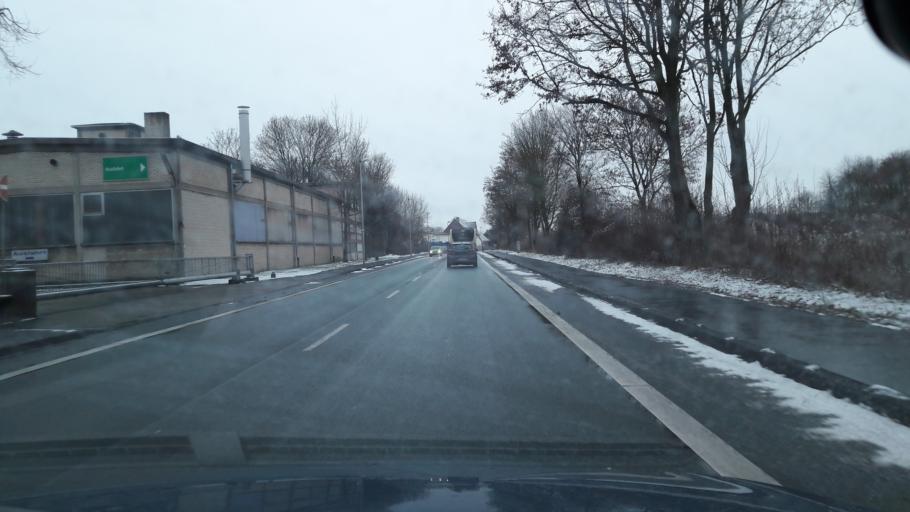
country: DE
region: North Rhine-Westphalia
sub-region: Regierungsbezirk Munster
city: Ennigerloh
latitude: 51.8231
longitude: 8.0252
